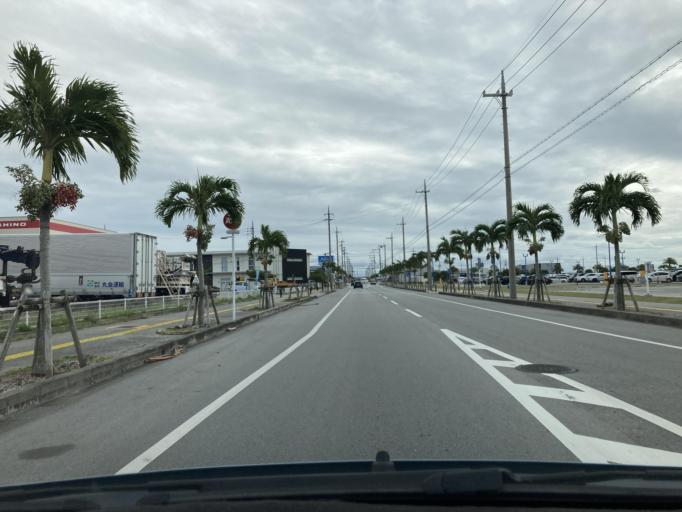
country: JP
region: Okinawa
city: Itoman
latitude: 26.1582
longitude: 127.6524
